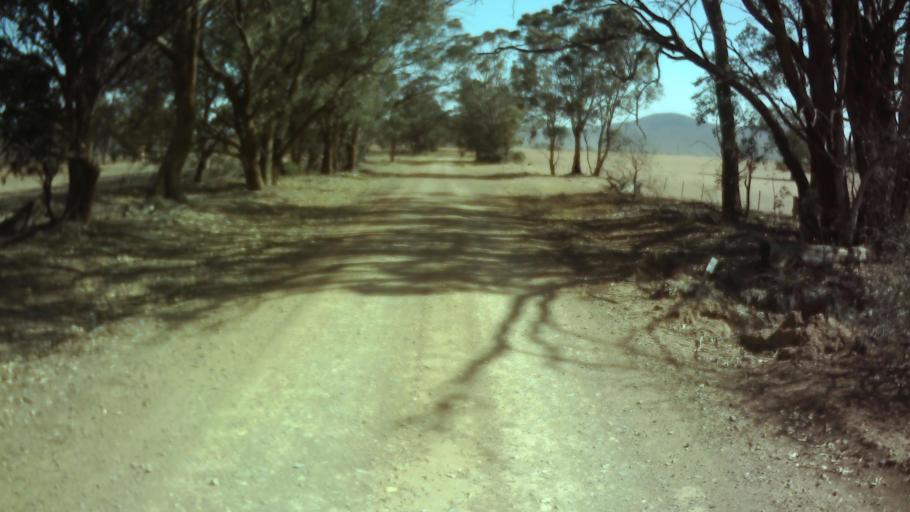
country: AU
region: New South Wales
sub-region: Weddin
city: Grenfell
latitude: -33.8443
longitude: 148.0175
